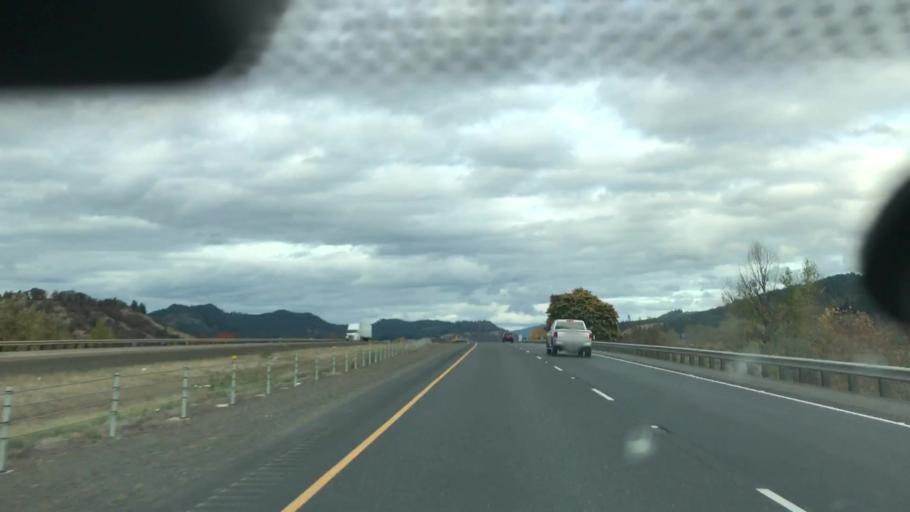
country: US
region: Oregon
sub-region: Douglas County
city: Yoncalla
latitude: 43.5667
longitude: -123.2765
